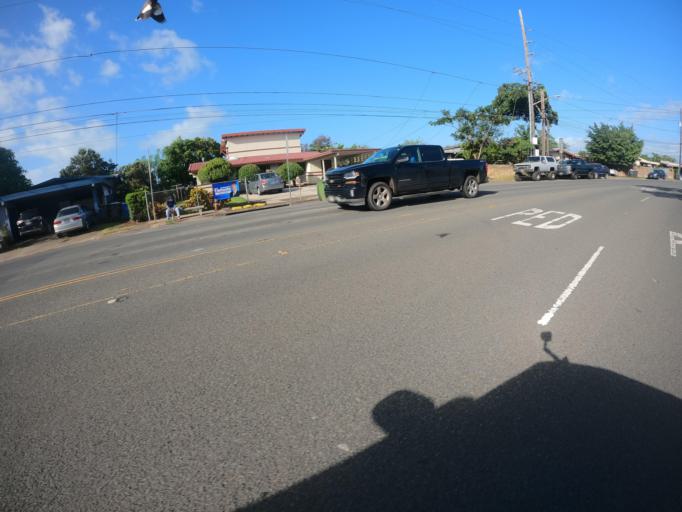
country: US
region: Hawaii
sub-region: Honolulu County
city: Halawa
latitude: 21.3734
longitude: -157.9202
